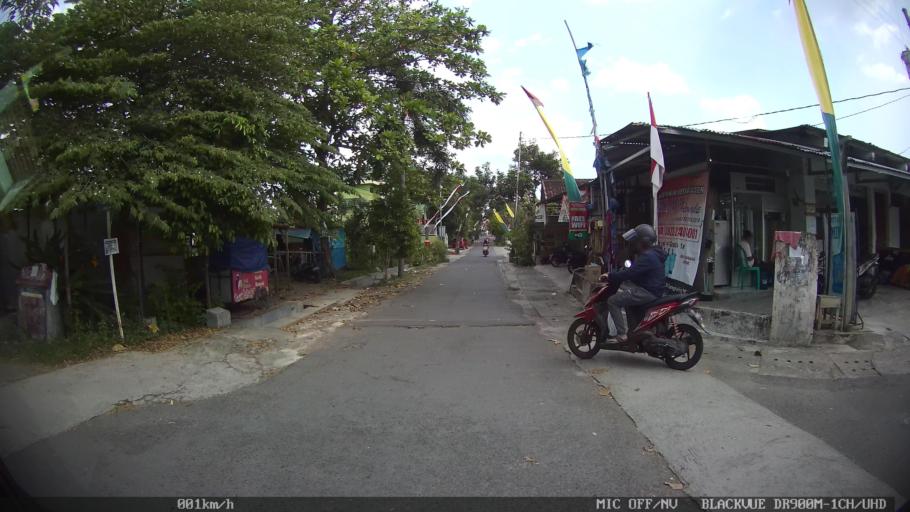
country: ID
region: Daerah Istimewa Yogyakarta
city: Yogyakarta
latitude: -7.8188
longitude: 110.4039
